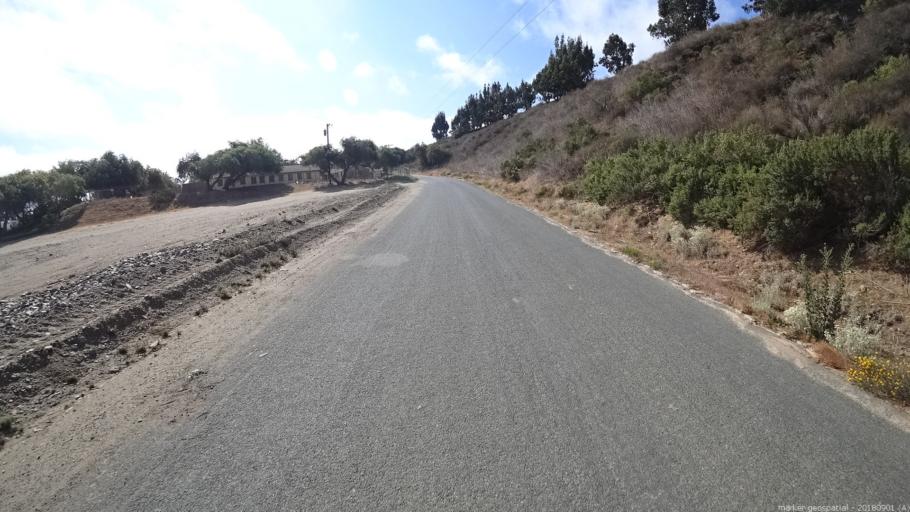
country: US
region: California
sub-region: Monterey County
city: Soledad
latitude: 36.3950
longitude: -121.3699
